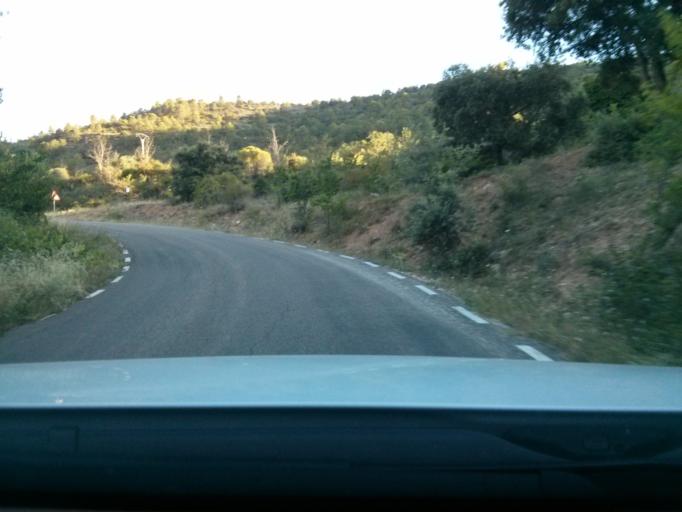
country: ES
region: Castille-La Mancha
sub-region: Provincia de Guadalajara
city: Mantiel
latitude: 40.6228
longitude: -2.6396
